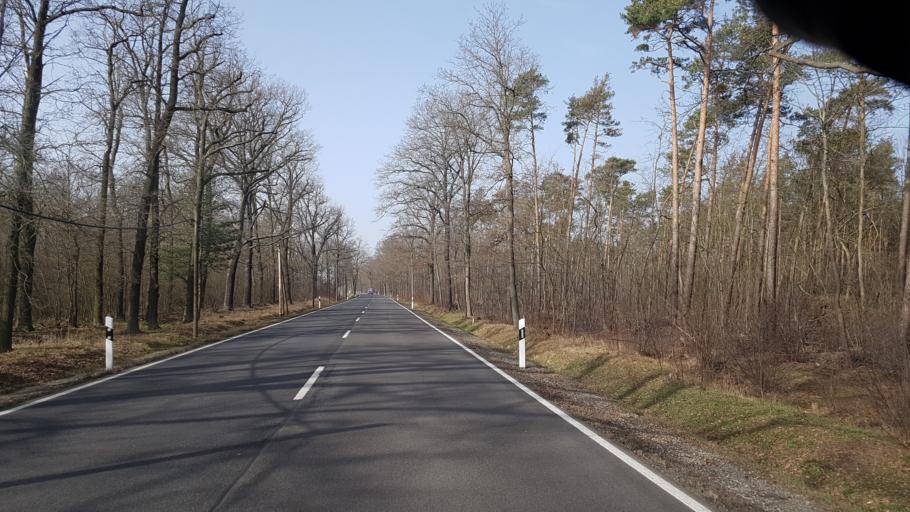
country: DE
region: Brandenburg
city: Cottbus
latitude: 51.7424
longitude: 14.3931
